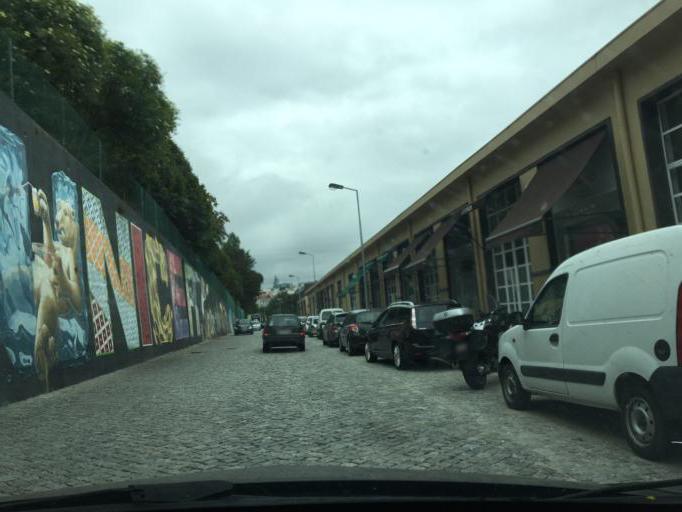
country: PT
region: Porto
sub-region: Maia
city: Leca do Bailio
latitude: 41.2155
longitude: -8.6240
